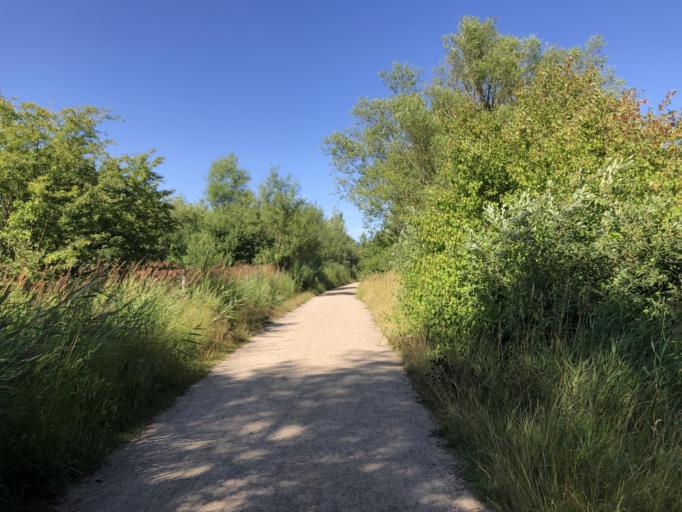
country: DK
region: Capital Region
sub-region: Kobenhavn
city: Christianshavn
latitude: 55.6558
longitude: 12.5794
